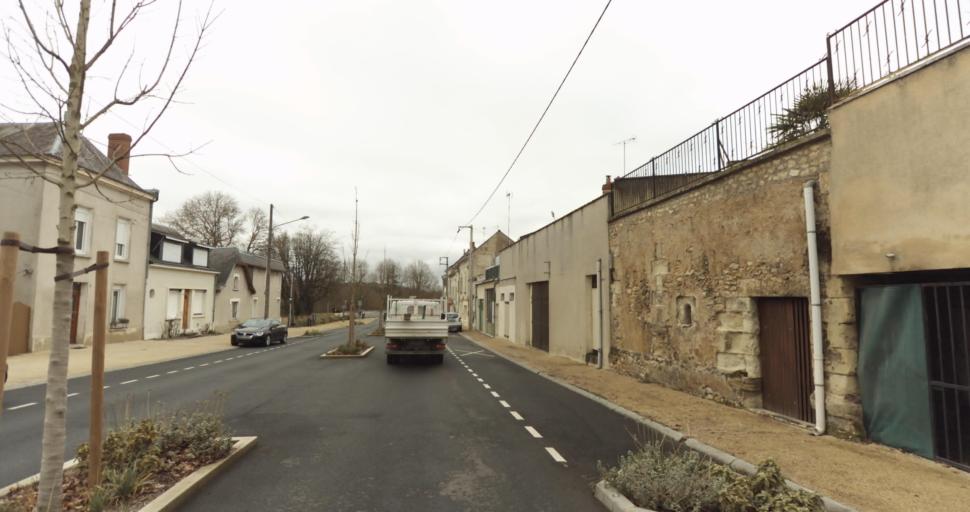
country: FR
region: Pays de la Loire
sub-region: Departement de Maine-et-Loire
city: Montreuil-Bellay
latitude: 47.1381
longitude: -0.1557
